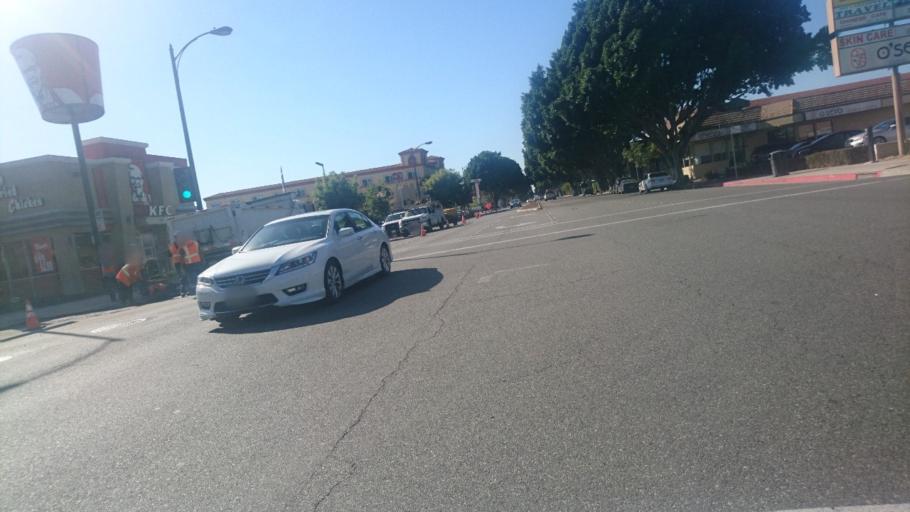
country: US
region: California
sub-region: Los Angeles County
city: East Pasadena
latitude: 34.1462
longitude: -118.0904
